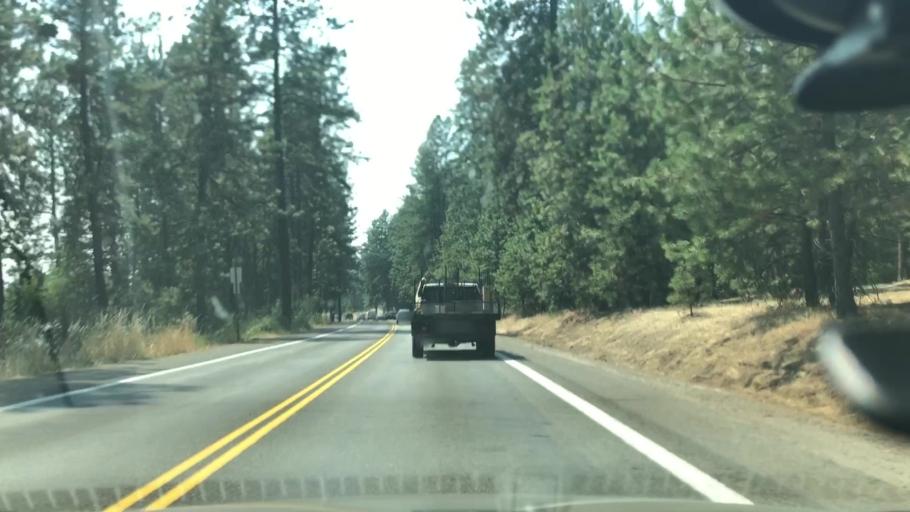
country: US
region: Washington
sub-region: Spokane County
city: Millwood
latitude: 47.6944
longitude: -117.3112
